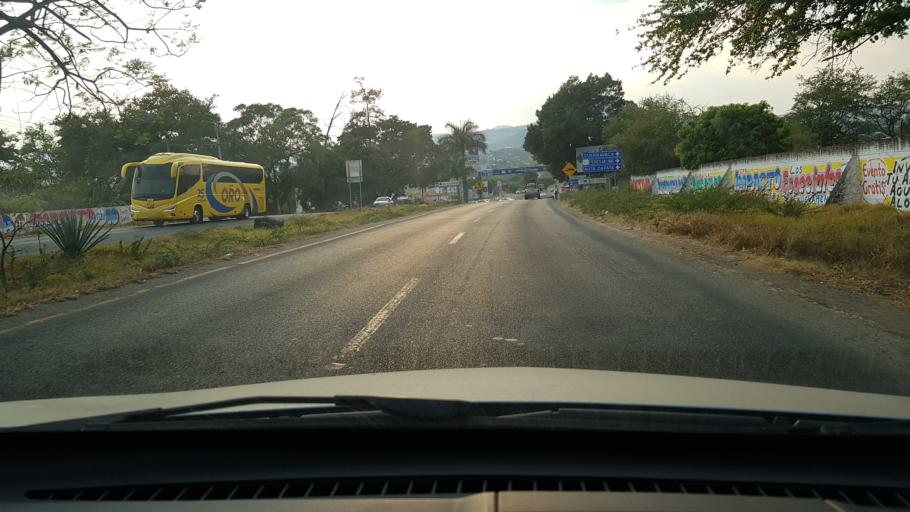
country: MX
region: Morelos
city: Yautepec
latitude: 18.8702
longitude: -99.0657
